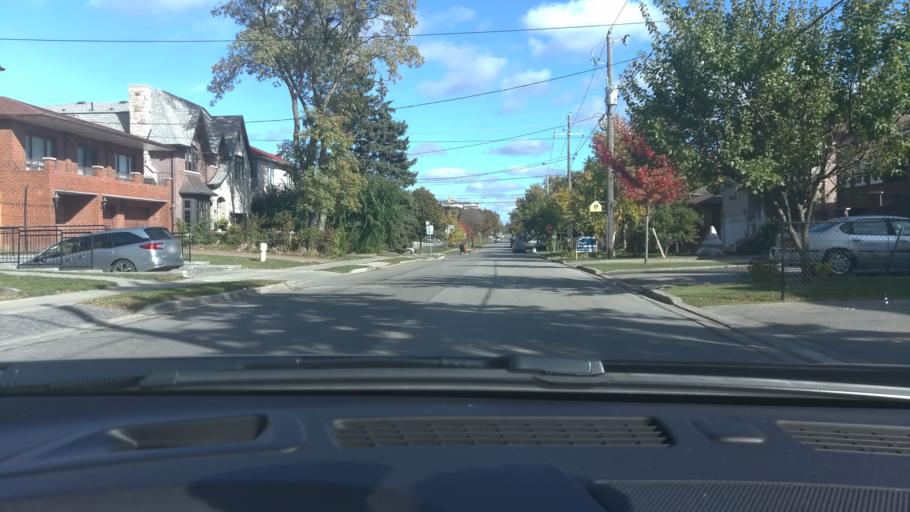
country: CA
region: Ontario
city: Toronto
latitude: 43.7123
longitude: -79.4373
